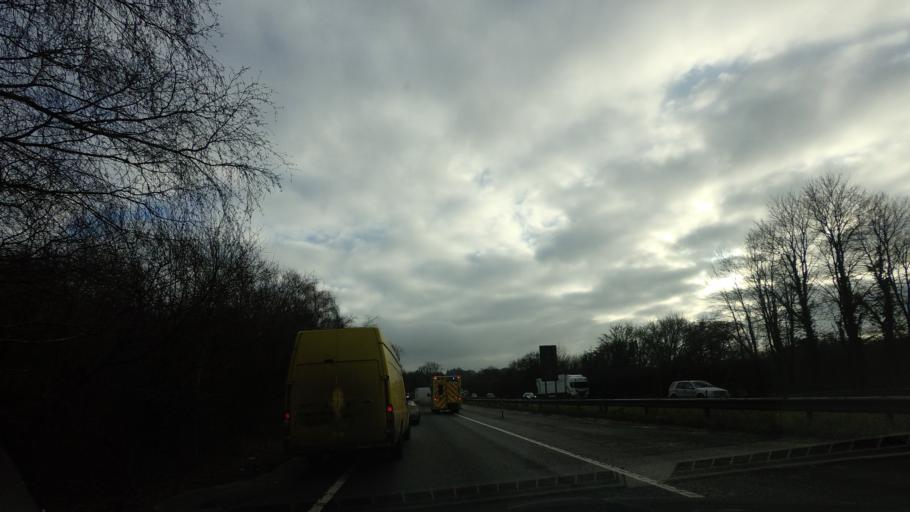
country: GB
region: England
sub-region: Kent
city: Hawkhurst
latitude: 51.0609
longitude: 0.4448
